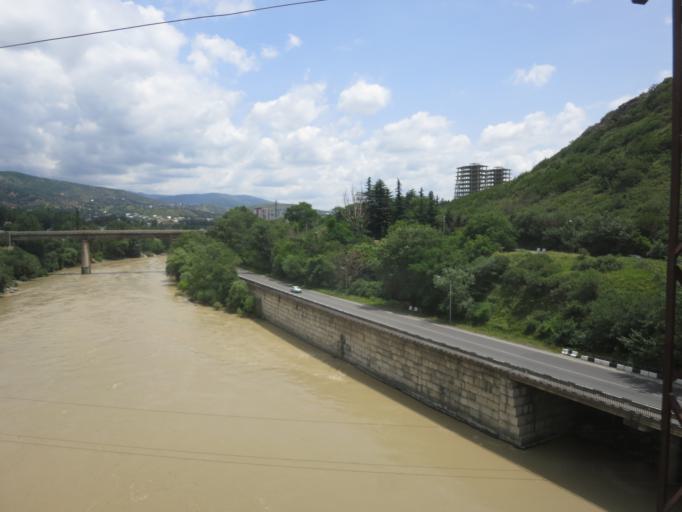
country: GE
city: Zahesi
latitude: 41.8236
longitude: 44.7650
